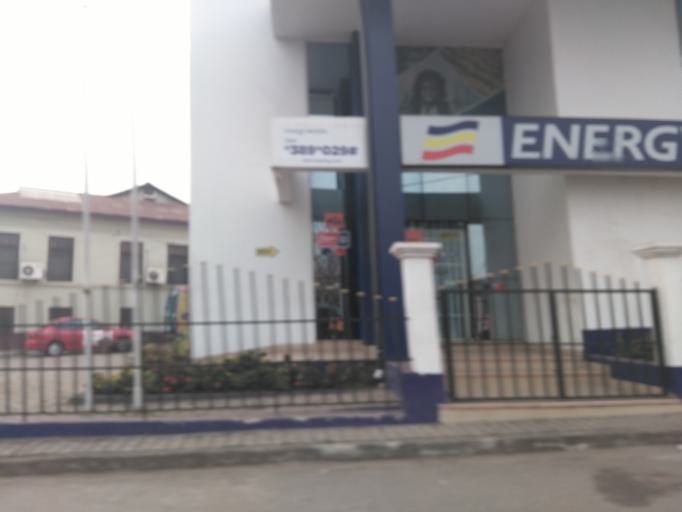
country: GH
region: Ashanti
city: Kumasi
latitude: 6.7032
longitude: -1.6143
